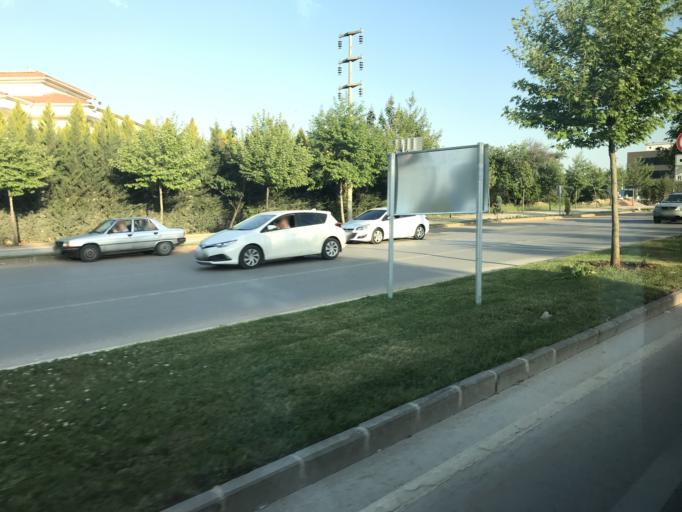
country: TR
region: Gaziantep
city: Sahinbey
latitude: 37.0620
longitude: 37.3205
